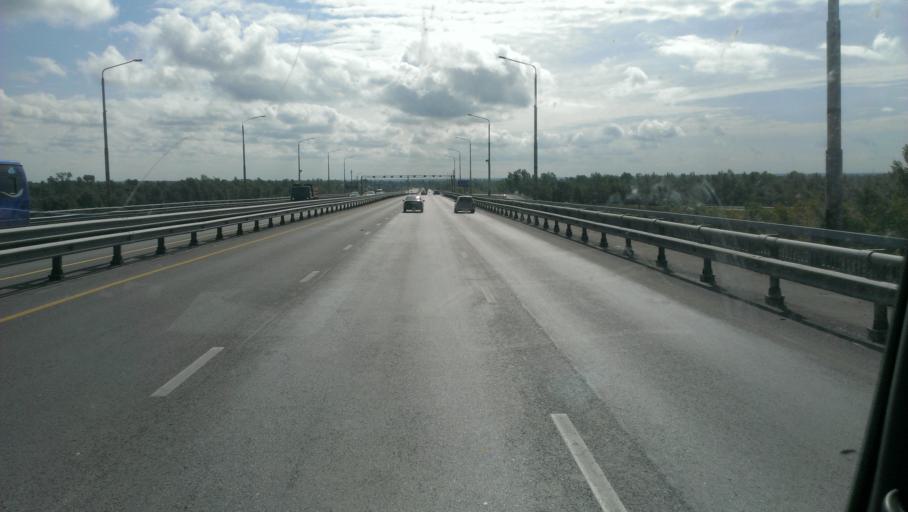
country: RU
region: Altai Krai
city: Zaton
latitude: 53.3217
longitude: 83.8081
